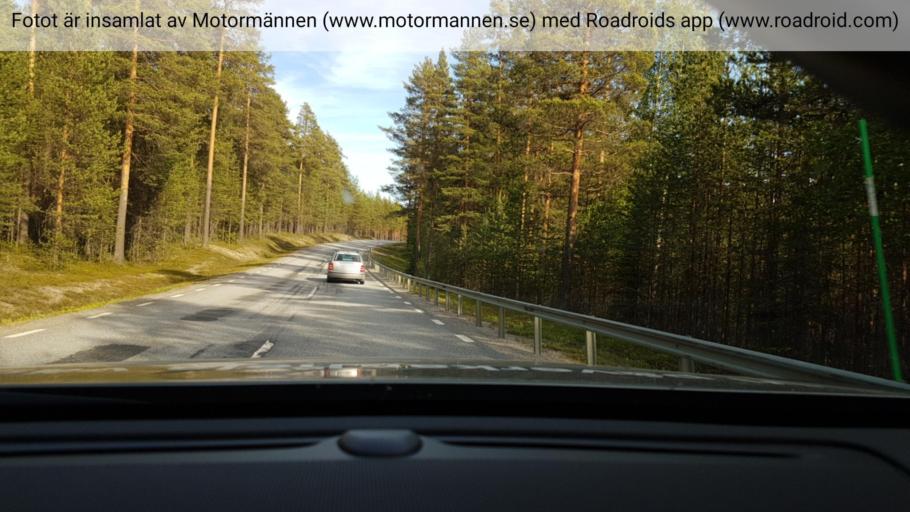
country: SE
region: Vaesterbotten
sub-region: Vindelns Kommun
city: Vindeln
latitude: 64.2474
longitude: 19.6483
